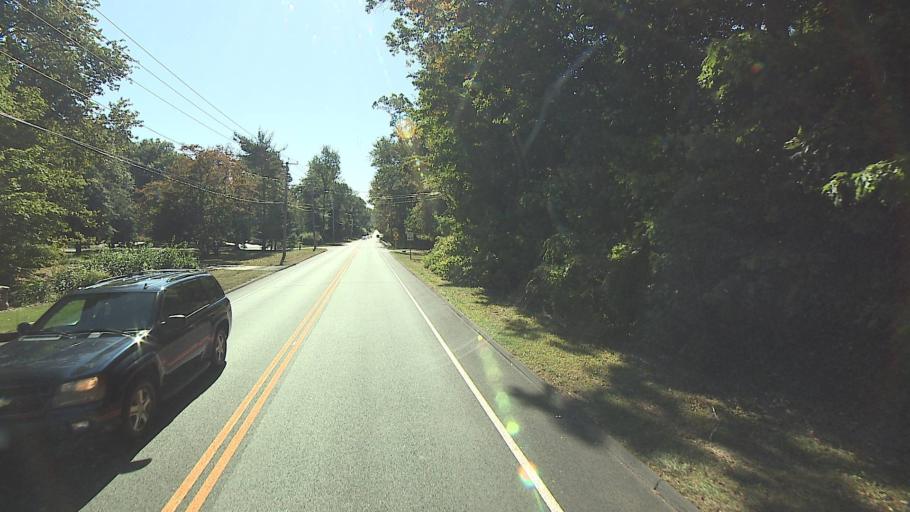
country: US
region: Connecticut
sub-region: New Haven County
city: Orange
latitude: 41.2738
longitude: -73.0045
